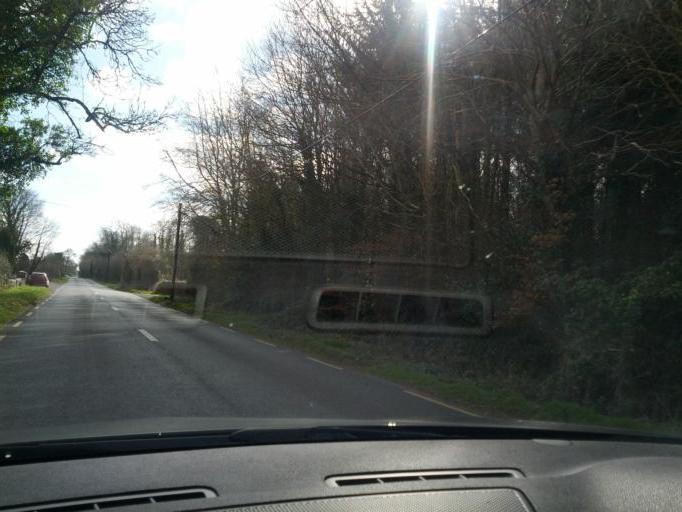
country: IE
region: Connaught
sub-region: County Galway
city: Ballinasloe
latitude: 53.4170
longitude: -8.3738
